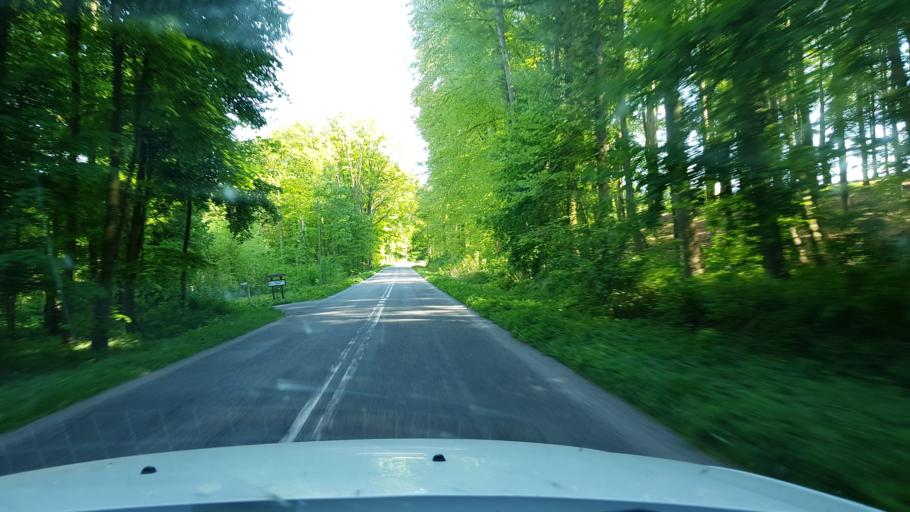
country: PL
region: West Pomeranian Voivodeship
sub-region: Powiat lobeski
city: Resko
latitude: 53.8352
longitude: 15.3839
